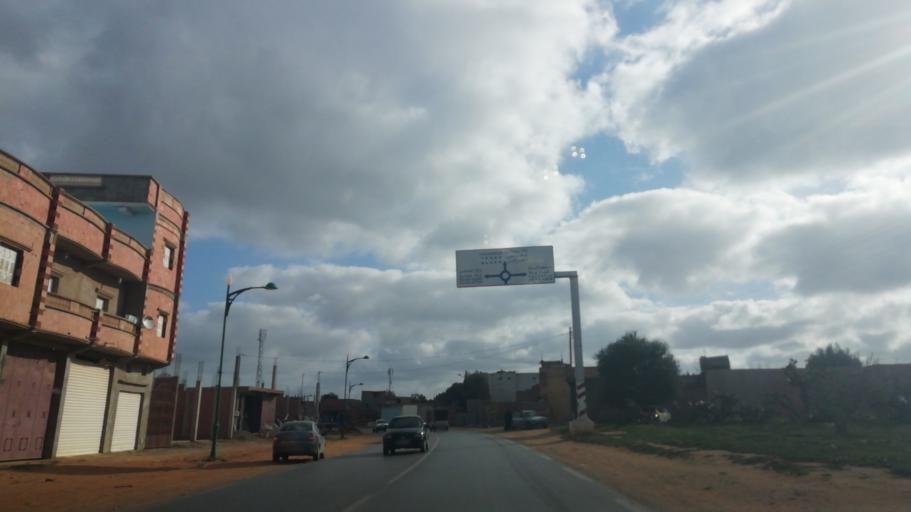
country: DZ
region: Relizane
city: Mazouna
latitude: 36.2611
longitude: 0.6123
